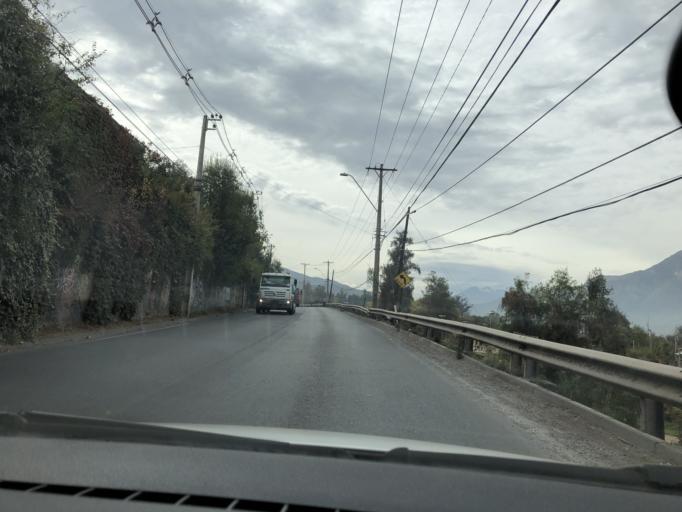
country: CL
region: Santiago Metropolitan
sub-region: Provincia de Cordillera
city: Puente Alto
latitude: -33.6068
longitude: -70.5357
